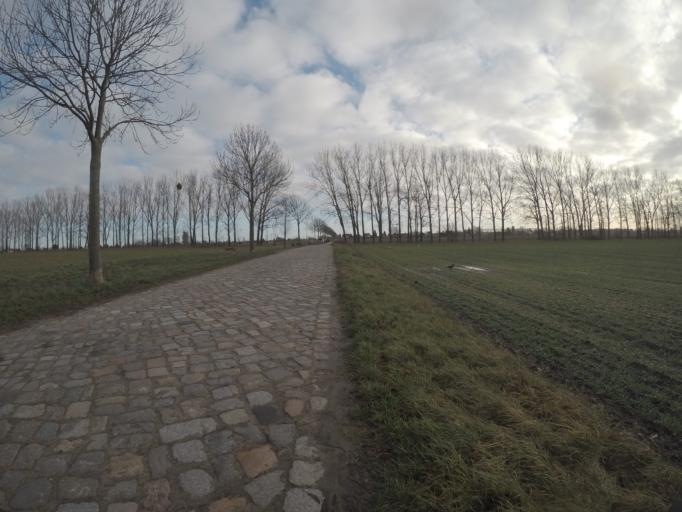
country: DE
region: Berlin
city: Wartenberg
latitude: 52.5898
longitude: 13.5249
